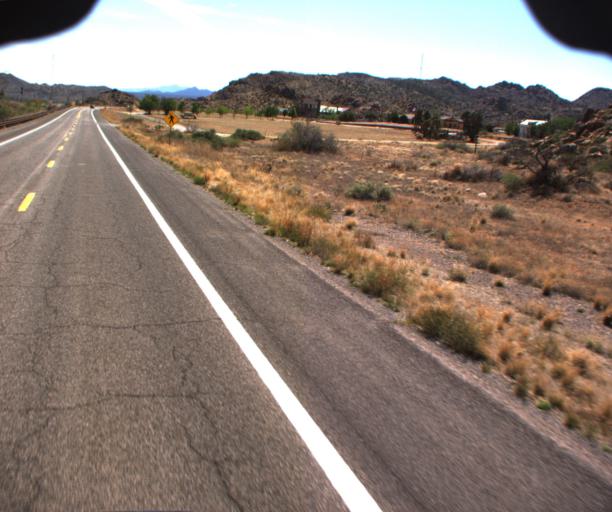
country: US
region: Arizona
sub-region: Mohave County
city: Peach Springs
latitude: 35.3891
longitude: -113.6579
